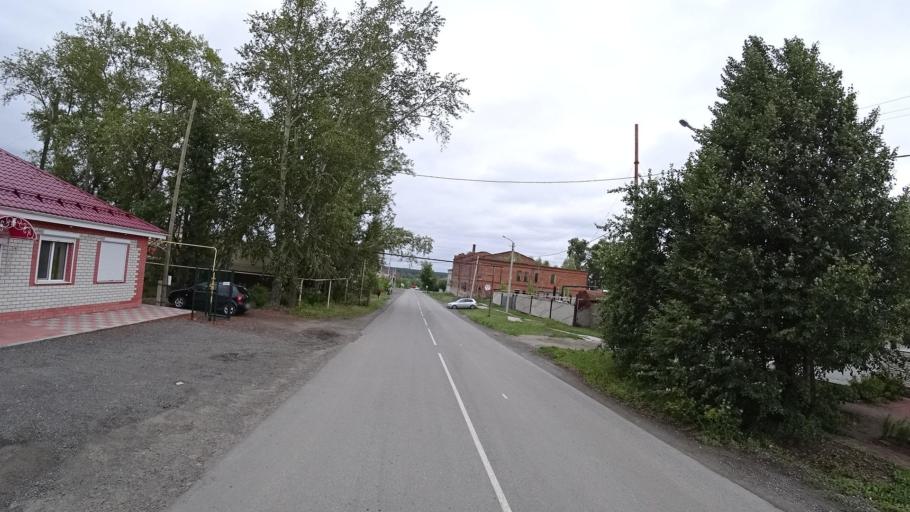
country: RU
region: Sverdlovsk
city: Kamyshlov
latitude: 56.8481
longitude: 62.6958
